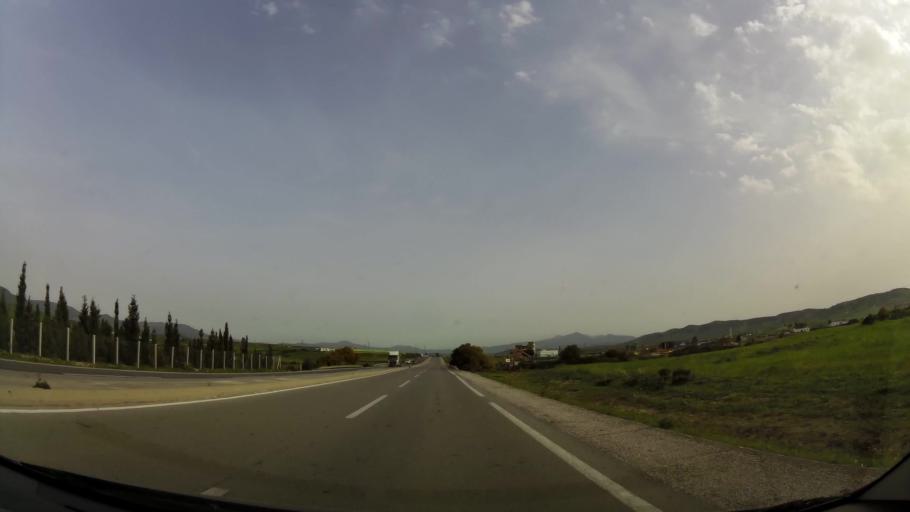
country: MA
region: Tanger-Tetouan
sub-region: Tanger-Assilah
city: Dar Chaoui
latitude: 35.6262
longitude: -5.6725
